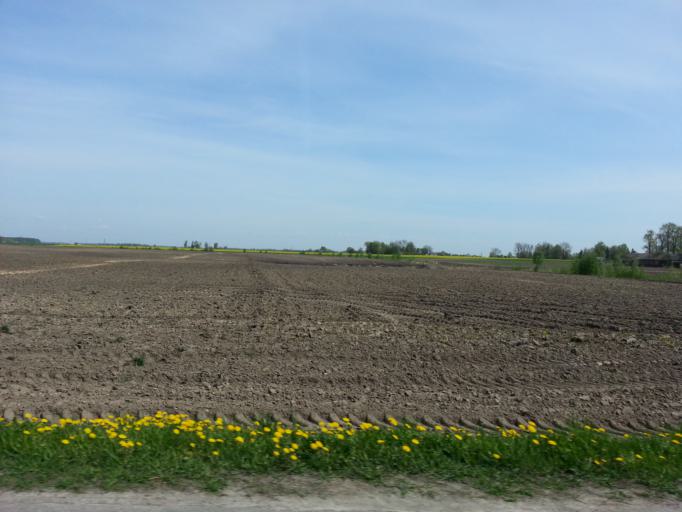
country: LT
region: Panevezys
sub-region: Panevezys City
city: Panevezys
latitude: 55.8693
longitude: 24.2364
